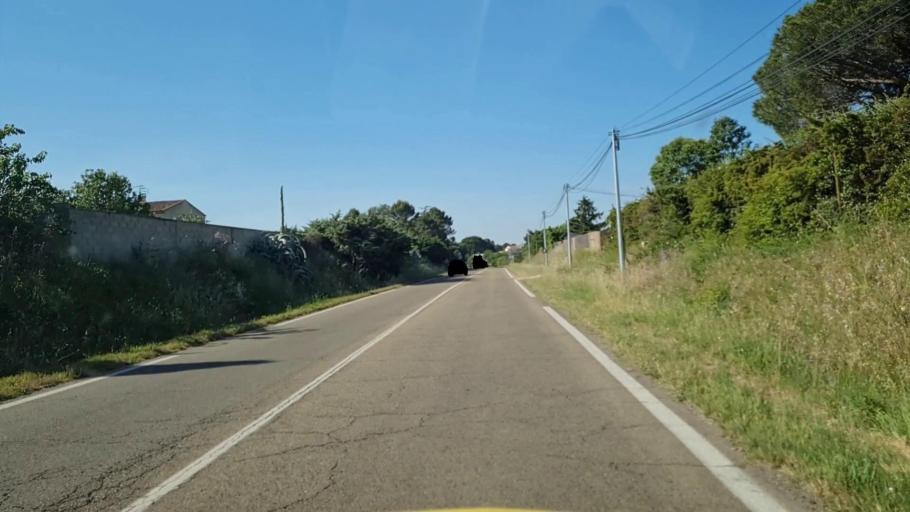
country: FR
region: Languedoc-Roussillon
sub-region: Departement du Gard
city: Saint-Gilles
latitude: 43.6904
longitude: 4.4276
